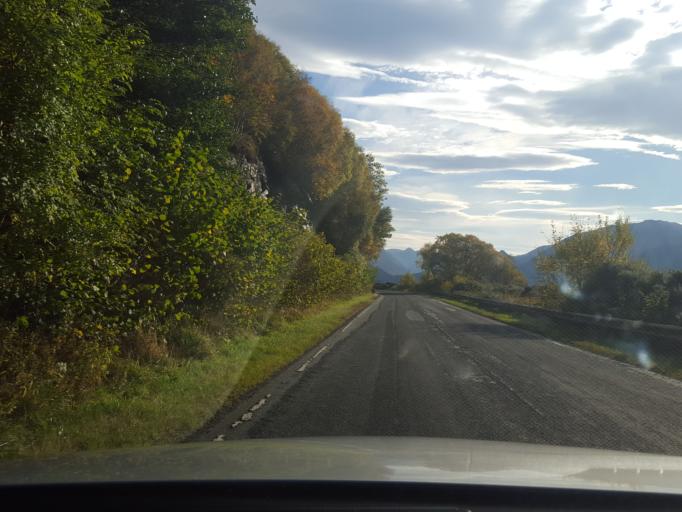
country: GB
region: Scotland
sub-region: Highland
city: Fort William
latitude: 57.2636
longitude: -5.5009
